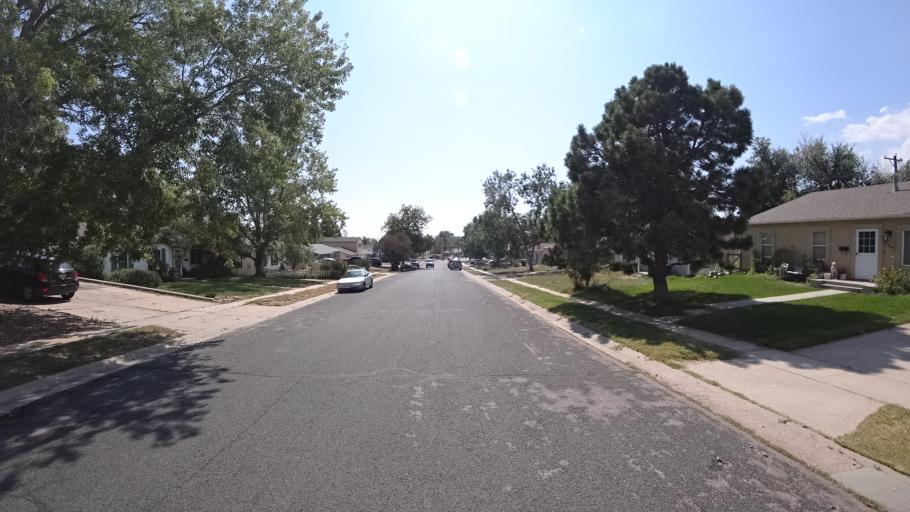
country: US
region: Colorado
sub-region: El Paso County
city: Colorado Springs
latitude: 38.8343
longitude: -104.7737
